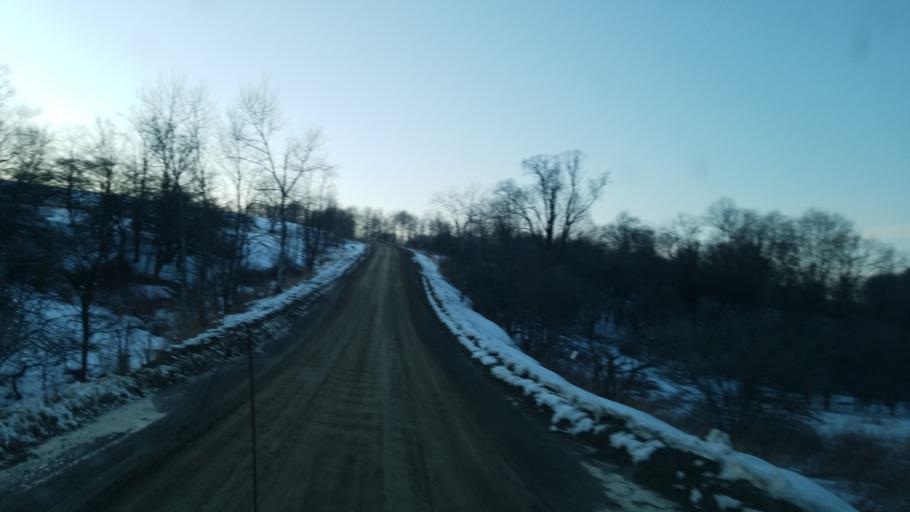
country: US
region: New York
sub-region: Allegany County
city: Andover
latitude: 42.0074
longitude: -77.7235
